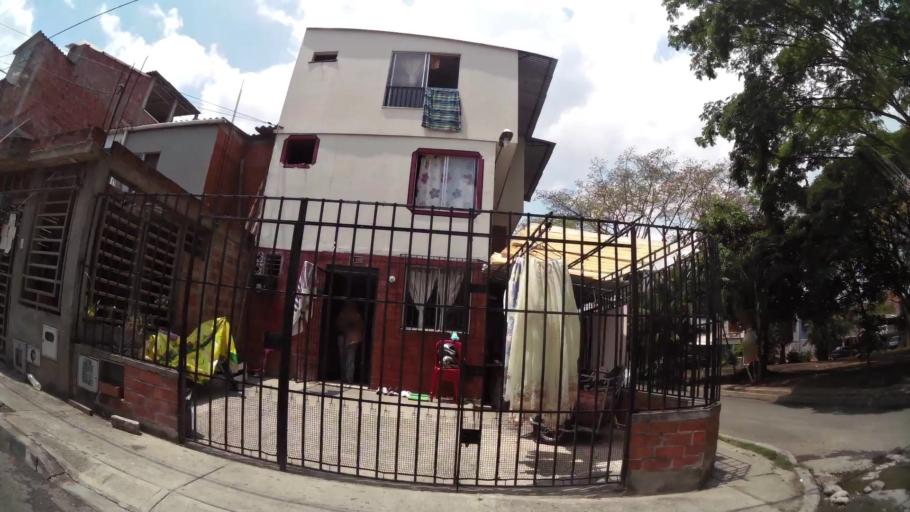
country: CO
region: Valle del Cauca
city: Cali
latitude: 3.4555
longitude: -76.4683
